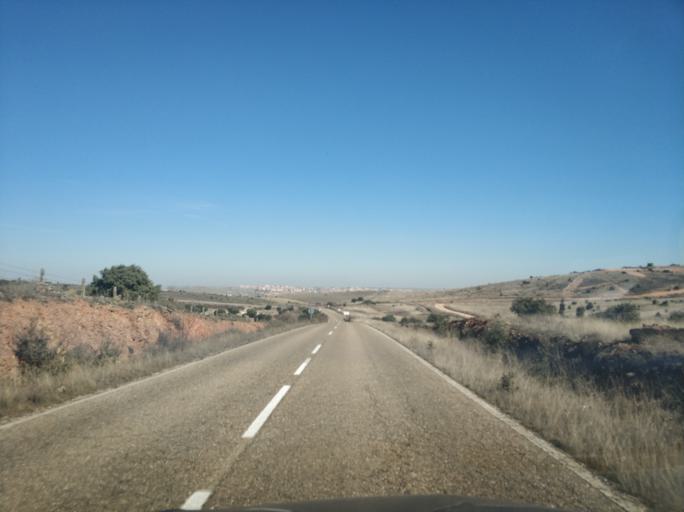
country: ES
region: Castille and Leon
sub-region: Provincia de Salamanca
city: Aldeatejada
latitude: 40.9344
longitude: -5.7227
